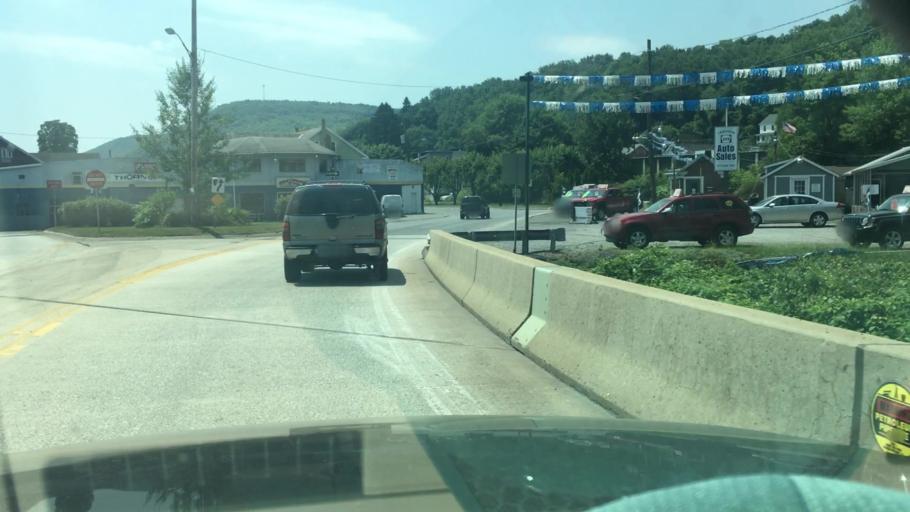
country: US
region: Pennsylvania
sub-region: Schuylkill County
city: Tamaqua
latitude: 40.8054
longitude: -75.9714
